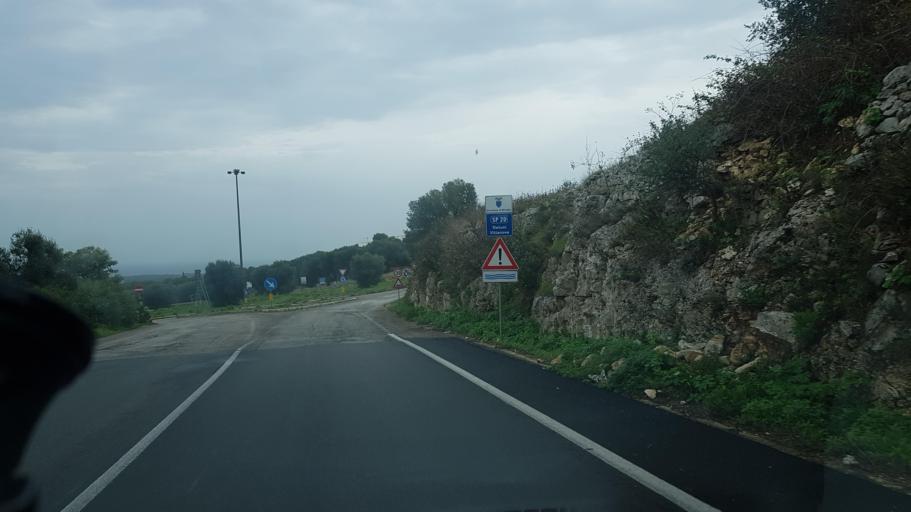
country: IT
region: Apulia
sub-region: Provincia di Brindisi
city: Ostuni
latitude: 40.7392
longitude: 17.5761
